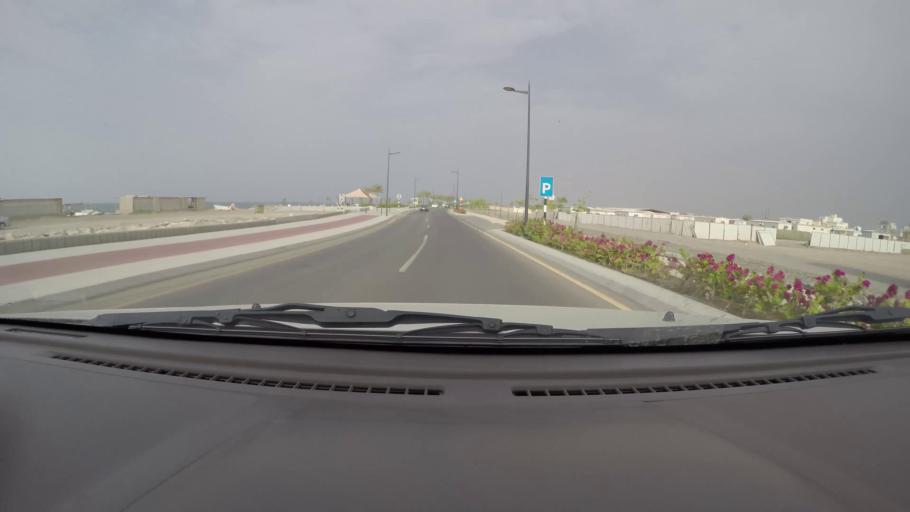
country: OM
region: Muhafazat Masqat
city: As Sib al Jadidah
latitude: 23.6927
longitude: 58.1646
